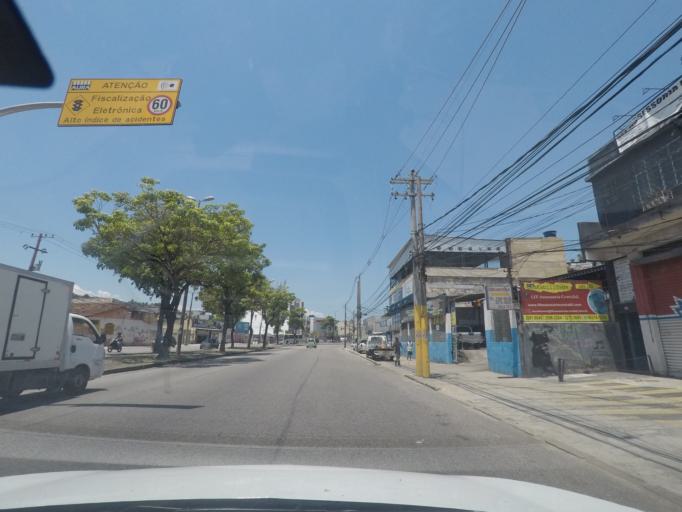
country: BR
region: Rio de Janeiro
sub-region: Rio De Janeiro
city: Rio de Janeiro
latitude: -22.8824
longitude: -43.2953
